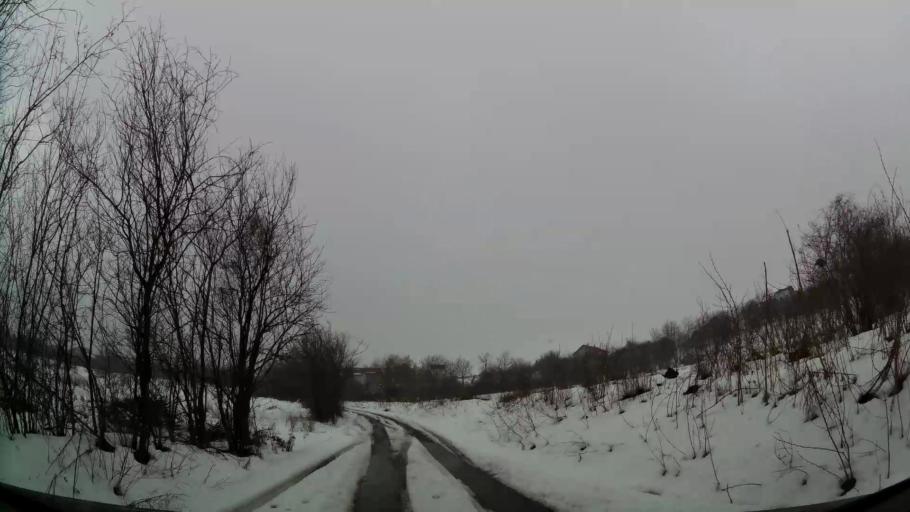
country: RS
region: Central Serbia
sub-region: Belgrade
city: Zvezdara
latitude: 44.7498
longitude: 20.5225
